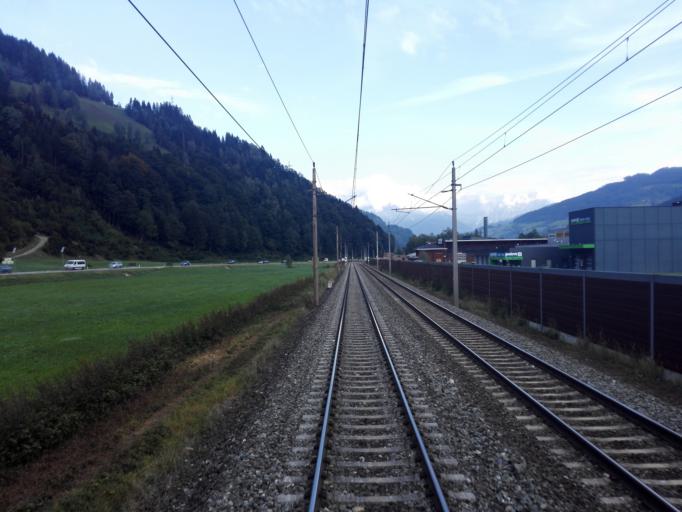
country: AT
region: Salzburg
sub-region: Politischer Bezirk Sankt Johann im Pongau
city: Sankt Johann im Pongau
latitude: 47.3713
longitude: 13.2074
